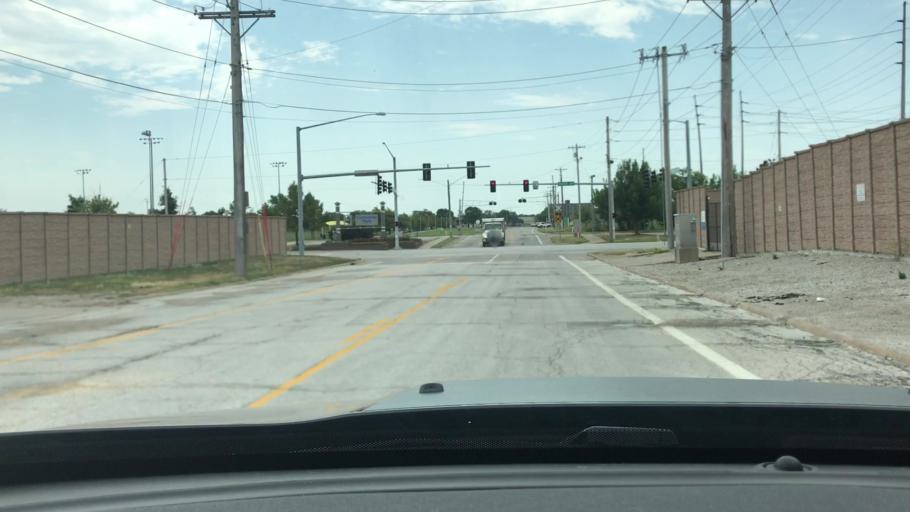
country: US
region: Iowa
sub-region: Scott County
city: Davenport
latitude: 41.5207
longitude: -90.5909
